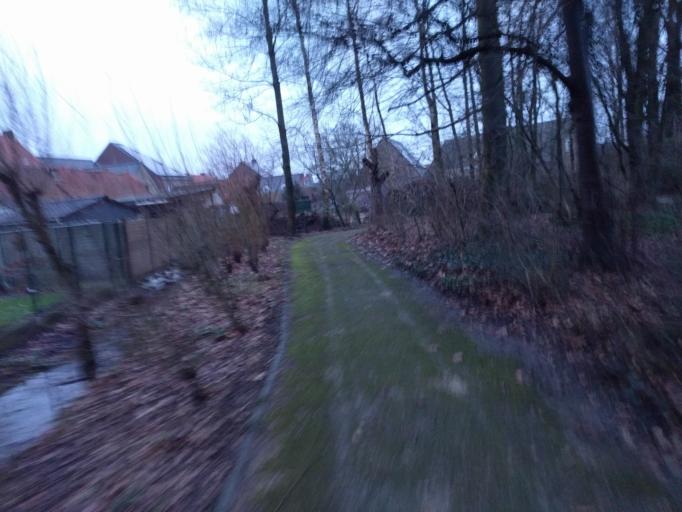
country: BE
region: Flanders
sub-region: Provincie West-Vlaanderen
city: Wevelgem
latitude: 50.8184
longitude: 3.1718
